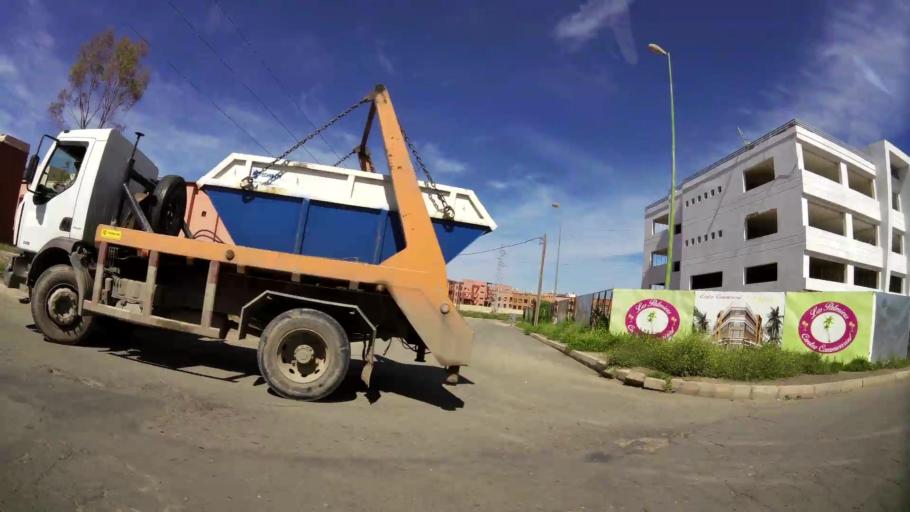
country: MA
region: Marrakech-Tensift-Al Haouz
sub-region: Marrakech
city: Marrakesh
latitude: 31.6424
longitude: -8.0425
